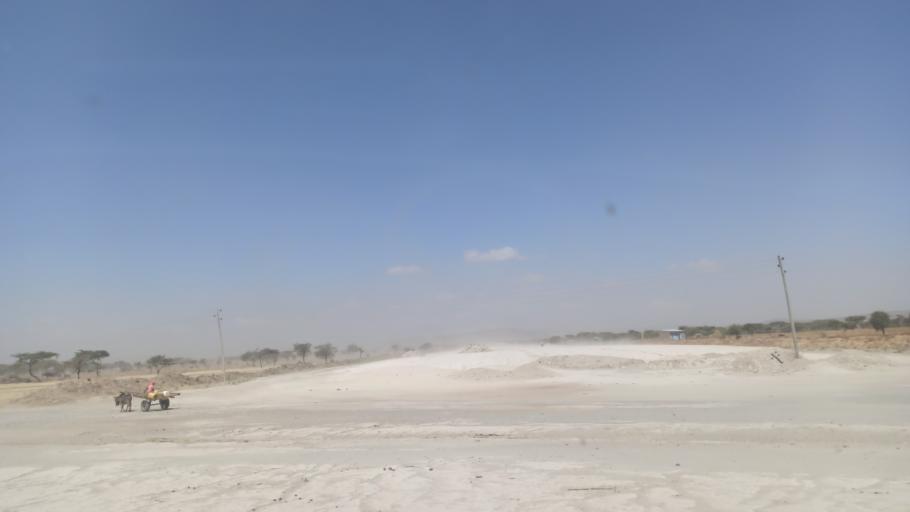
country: ET
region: Oromiya
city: Ziway
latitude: 7.7263
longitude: 38.6279
